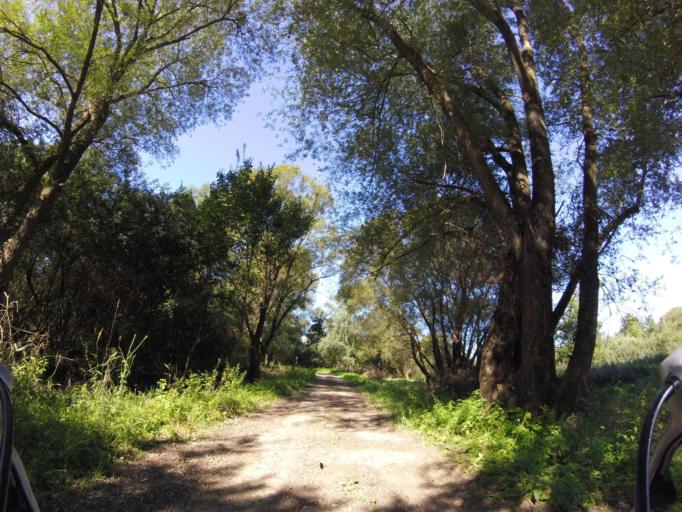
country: HU
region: Zala
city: Becsehely
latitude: 46.5456
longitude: 16.7359
